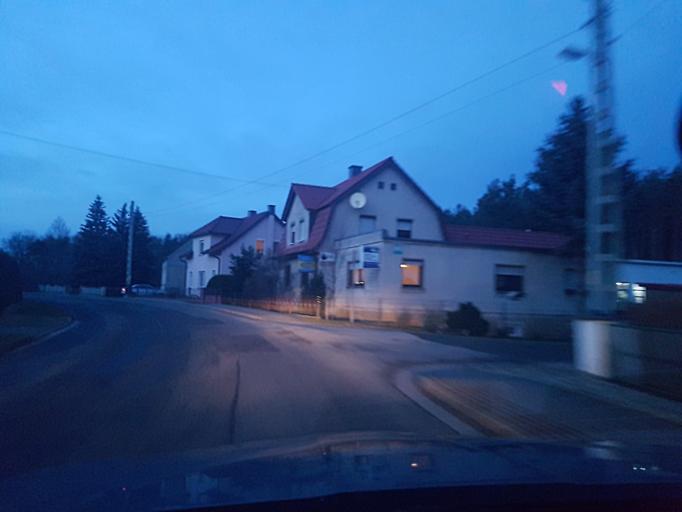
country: DE
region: Brandenburg
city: Bad Liebenwerda
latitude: 51.5529
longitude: 13.4242
